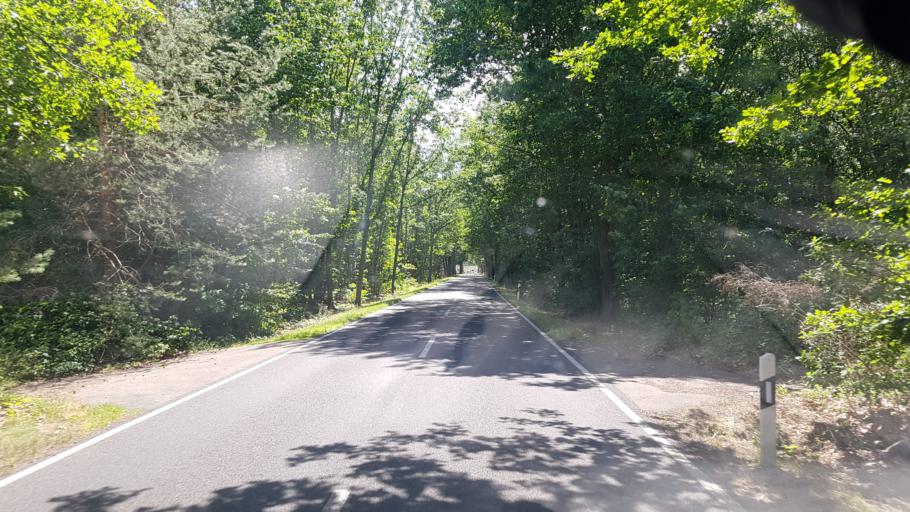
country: DE
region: Brandenburg
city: Sallgast
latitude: 51.5953
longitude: 13.8458
